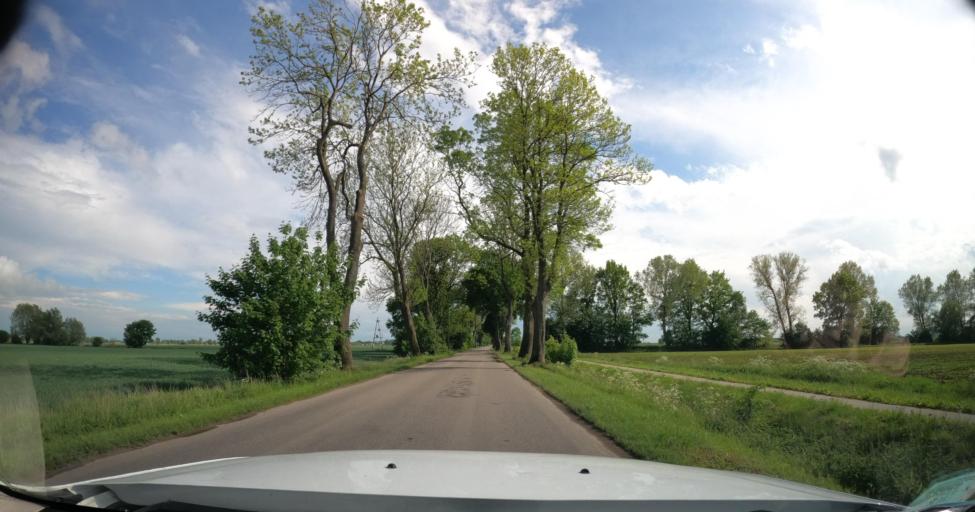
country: PL
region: Pomeranian Voivodeship
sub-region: Powiat nowodworski
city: Nowy Dwor Gdanski
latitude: 54.2040
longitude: 19.1376
